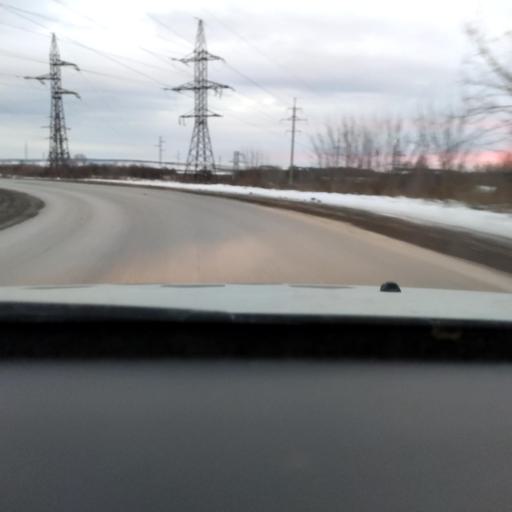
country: RU
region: Perm
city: Gamovo
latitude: 57.9212
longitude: 56.1026
